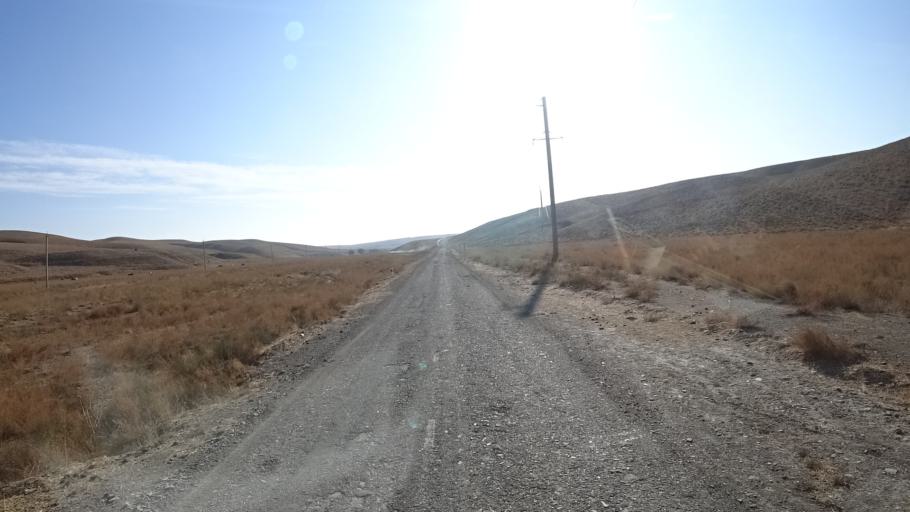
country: UZ
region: Navoiy
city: Karmana Shahri
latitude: 40.2772
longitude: 65.5811
